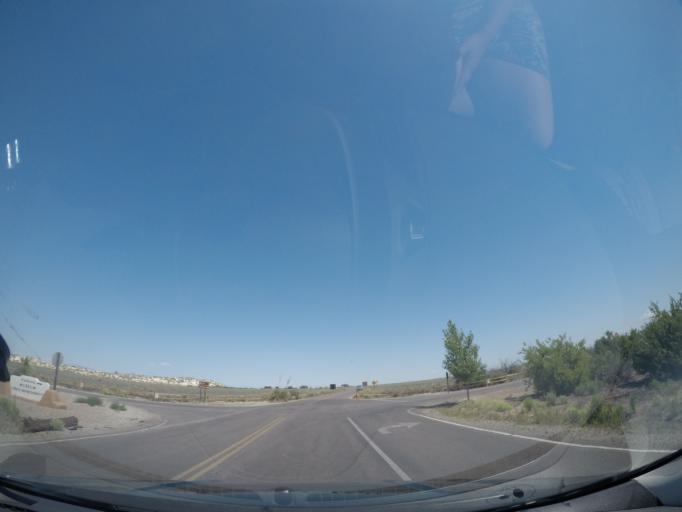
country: US
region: New Mexico
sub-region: Otero County
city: Holloman Air Force Base
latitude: 32.7796
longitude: -106.1732
